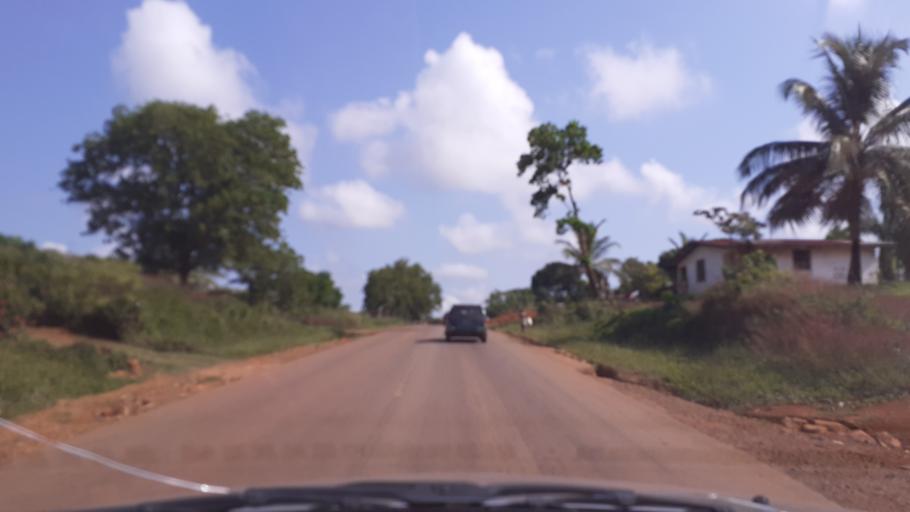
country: LR
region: Montserrado
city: Bensonville City
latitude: 6.2202
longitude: -10.5412
